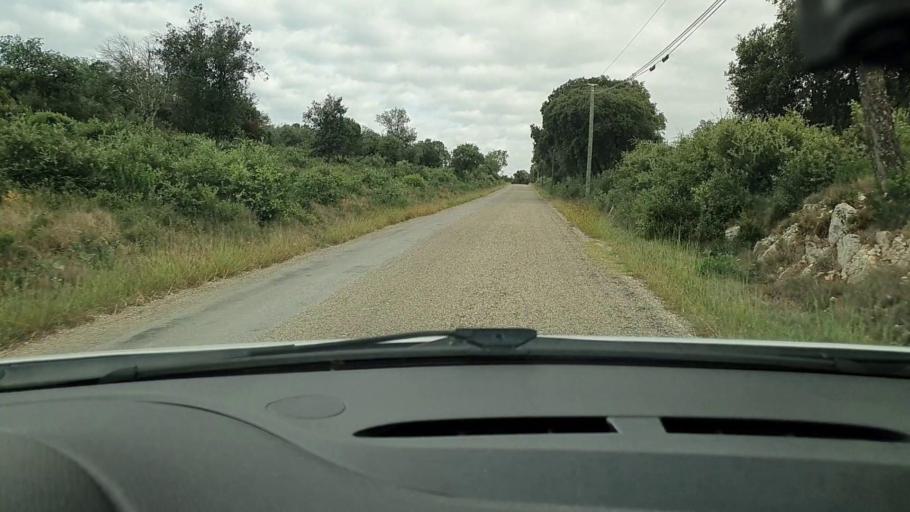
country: FR
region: Languedoc-Roussillon
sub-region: Departement du Gard
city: Montaren-et-Saint-Mediers
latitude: 44.0643
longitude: 4.3141
